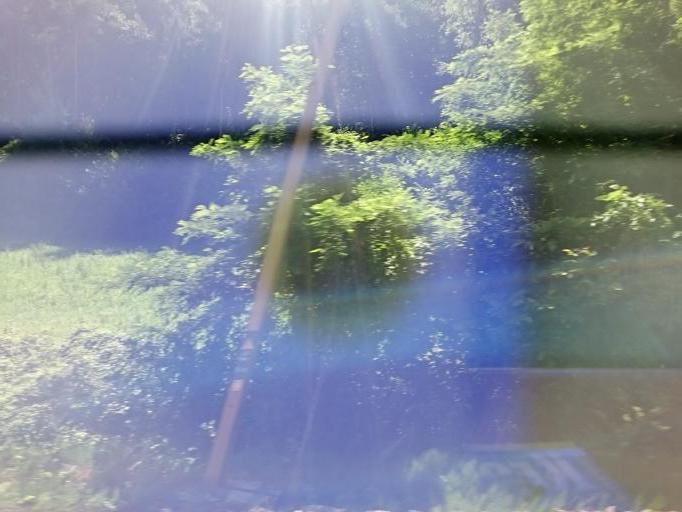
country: IT
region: Trentino-Alto Adige
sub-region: Bolzano
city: Chiusa
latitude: 46.6313
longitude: 11.5533
